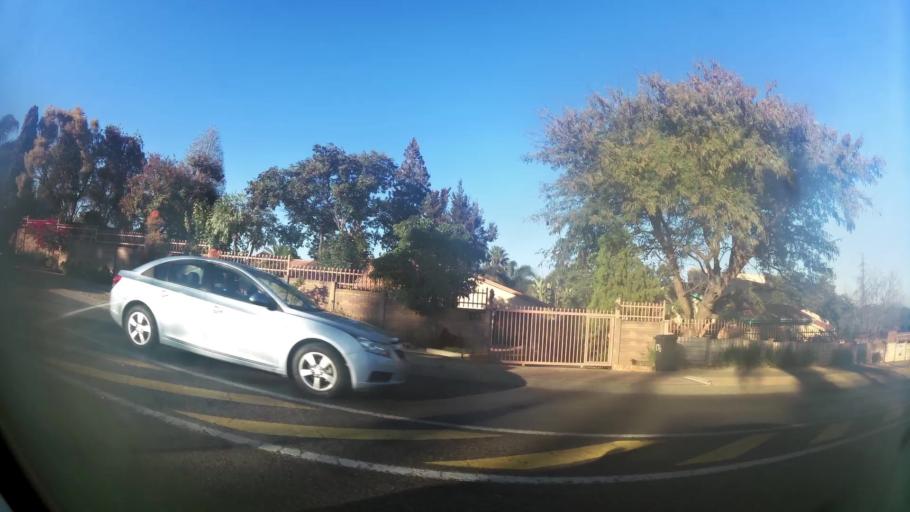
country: ZA
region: Gauteng
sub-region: City of Tshwane Metropolitan Municipality
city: Centurion
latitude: -25.8936
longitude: 28.1404
